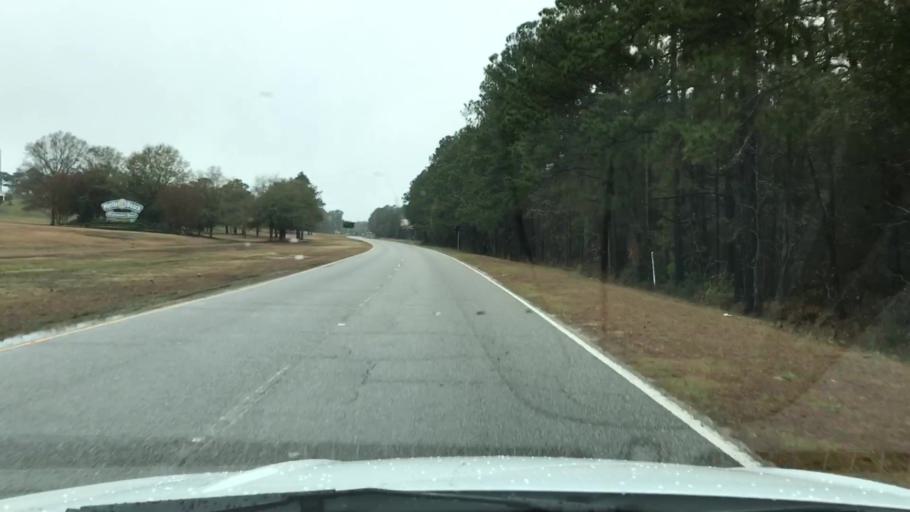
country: US
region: South Carolina
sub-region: Horry County
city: Myrtle Beach
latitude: 33.7698
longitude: -78.8044
